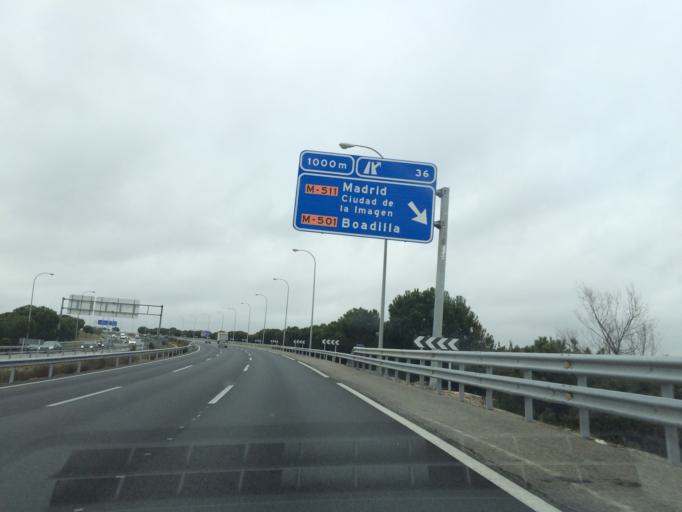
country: ES
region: Madrid
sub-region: Provincia de Madrid
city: Alcorcon
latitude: 40.3808
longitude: -3.8106
